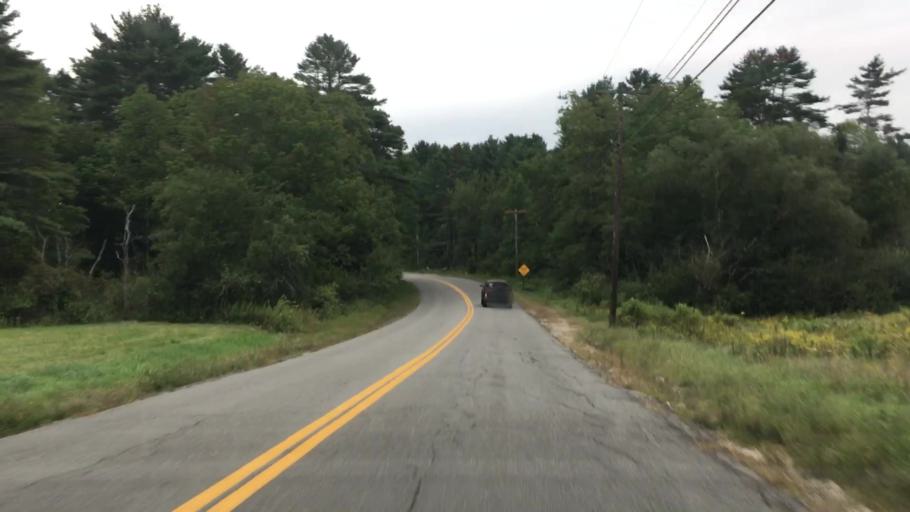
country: US
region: Maine
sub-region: Cumberland County
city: Freeport
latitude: 43.8863
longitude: -70.1709
